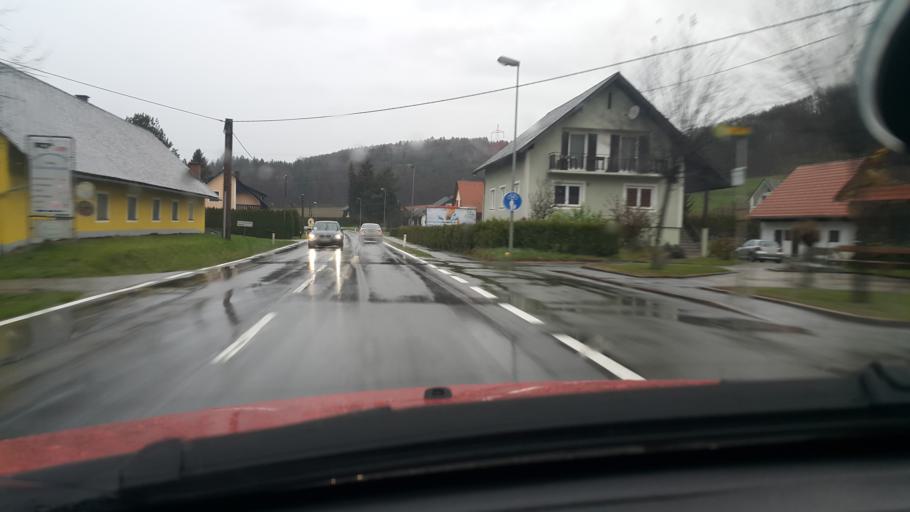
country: AT
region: Styria
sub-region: Politischer Bezirk Leibnitz
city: Weitendorf
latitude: 46.8686
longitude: 15.4862
